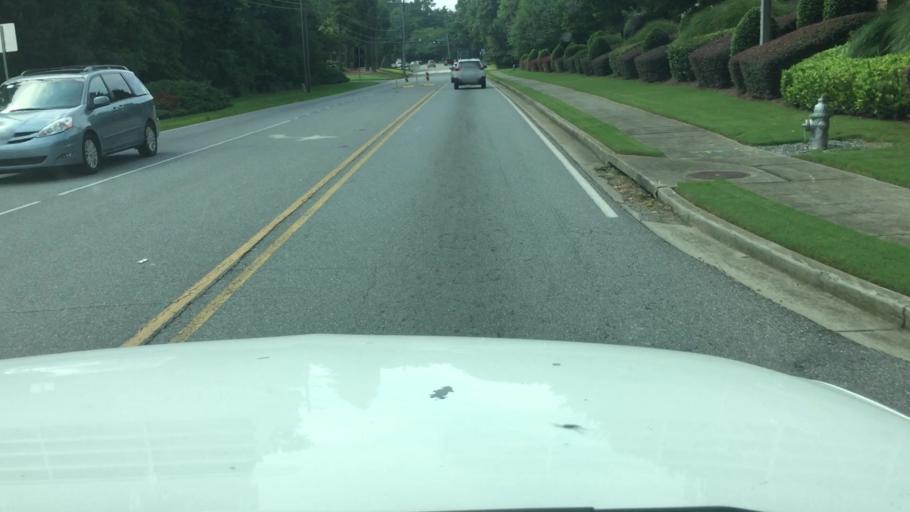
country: US
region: Georgia
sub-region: Fulton County
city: Johns Creek
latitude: 34.0963
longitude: -84.2111
